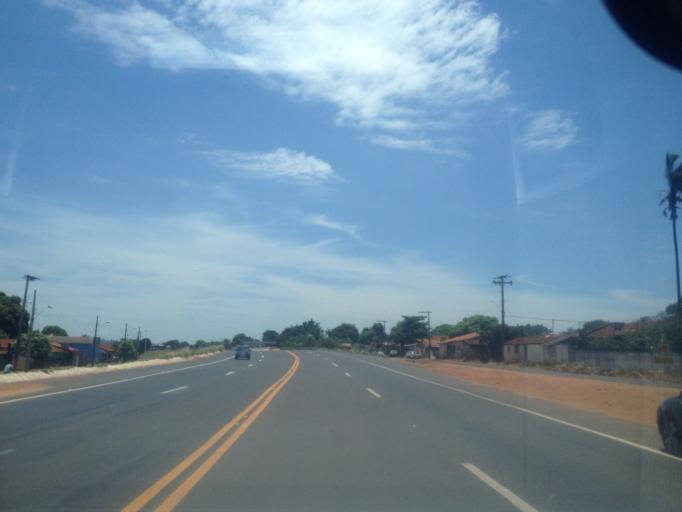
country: BR
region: Minas Gerais
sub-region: Monte Alegre De Minas
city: Monte Alegre de Minas
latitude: -18.8765
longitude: -48.8788
